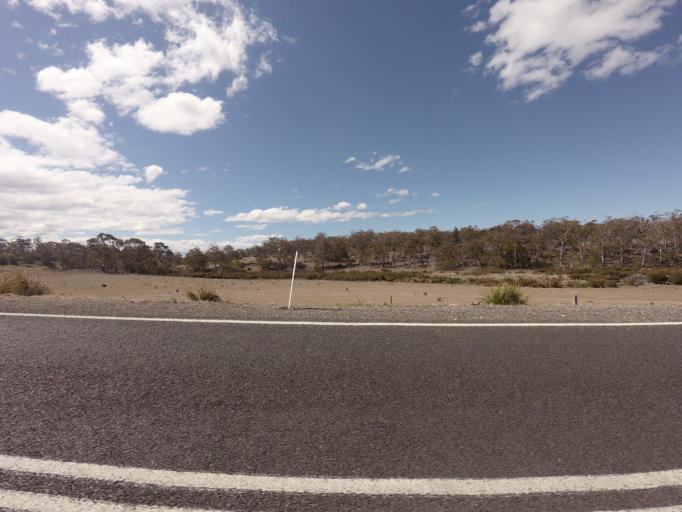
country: AU
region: Tasmania
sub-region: Break O'Day
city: St Helens
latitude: -42.0309
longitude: 148.0211
